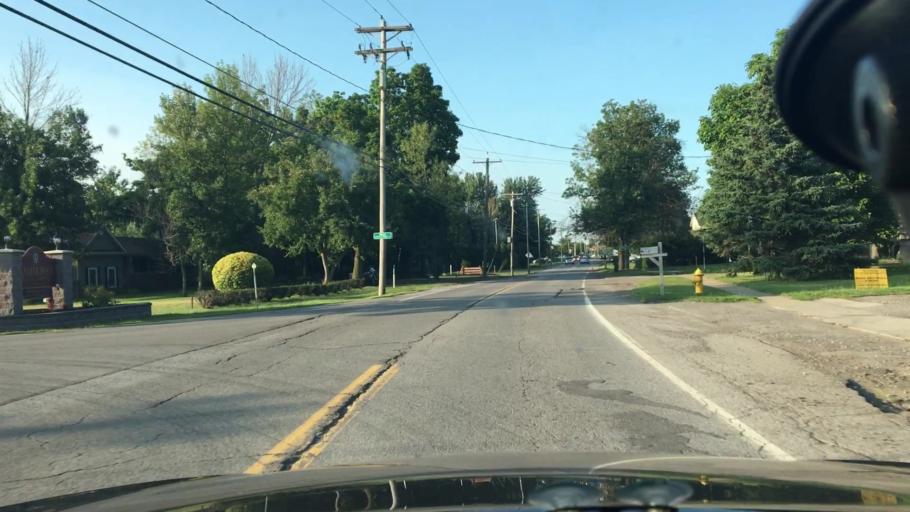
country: US
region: New York
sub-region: Erie County
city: Williamsville
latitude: 42.9851
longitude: -78.7639
